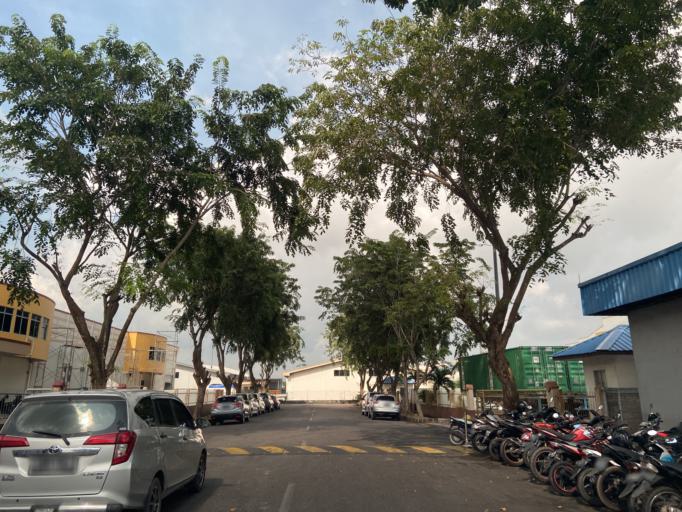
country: SG
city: Singapore
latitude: 1.1102
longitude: 104.0699
